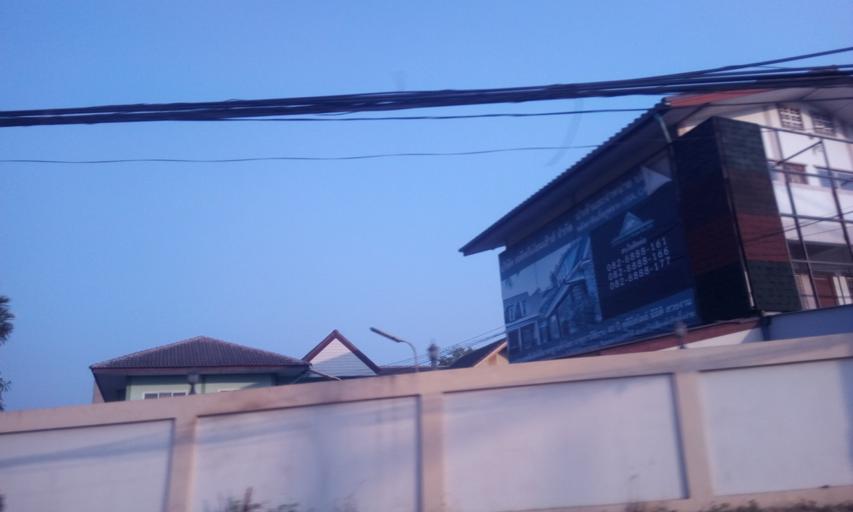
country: TH
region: Phra Nakhon Si Ayutthaya
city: Ban Bang Kadi Pathum Thani
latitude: 13.9968
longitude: 100.5550
